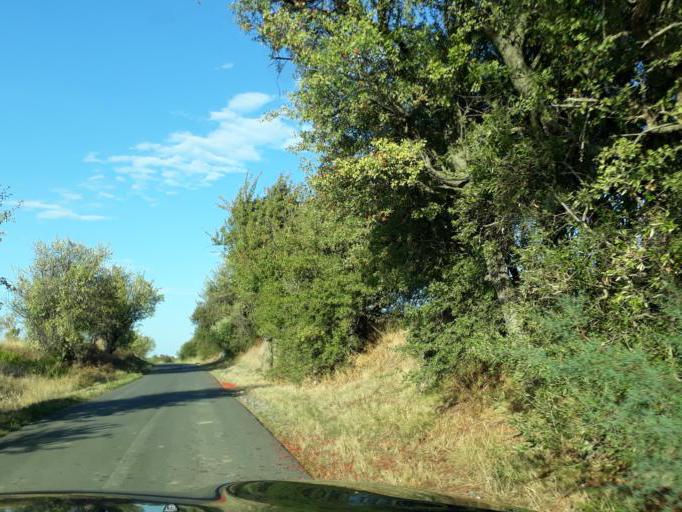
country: FR
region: Languedoc-Roussillon
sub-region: Departement de l'Herault
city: Florensac
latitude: 43.4028
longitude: 3.4714
